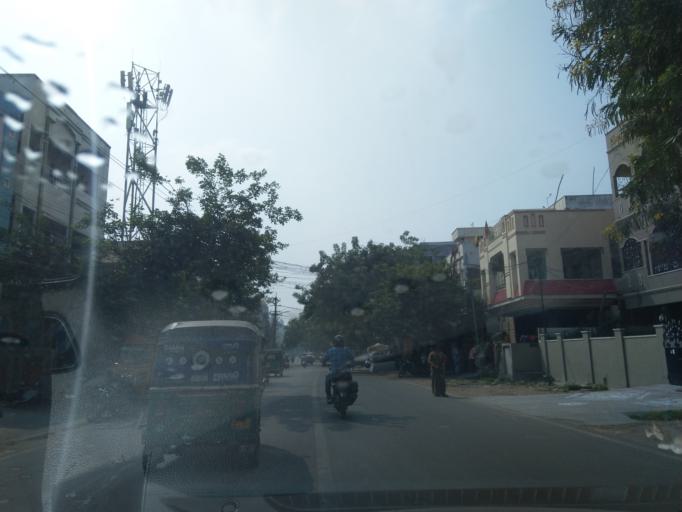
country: IN
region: Andhra Pradesh
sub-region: Krishna
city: Vijayawada
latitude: 16.5278
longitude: 80.6046
